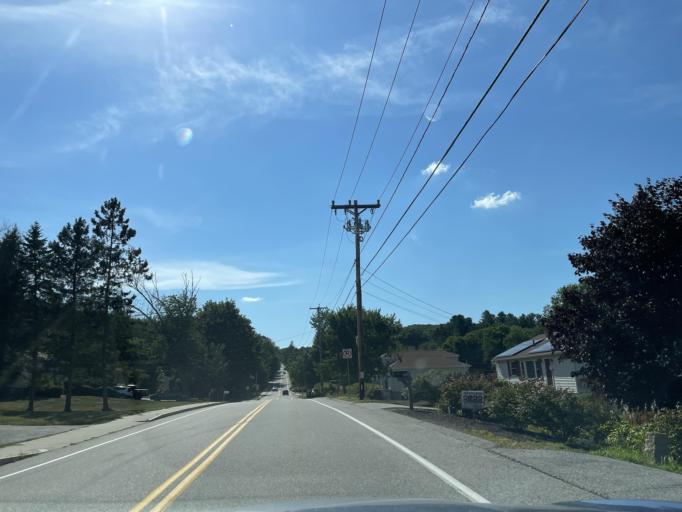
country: US
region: Massachusetts
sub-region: Worcester County
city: Northbridge
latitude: 42.1544
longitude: -71.6617
